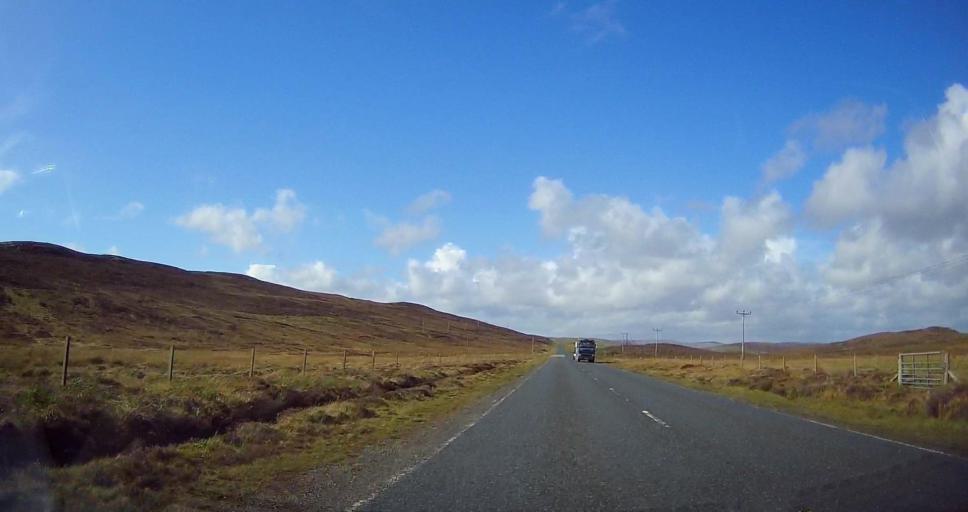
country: GB
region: Scotland
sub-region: Shetland Islands
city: Lerwick
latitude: 60.2079
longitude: -1.2334
